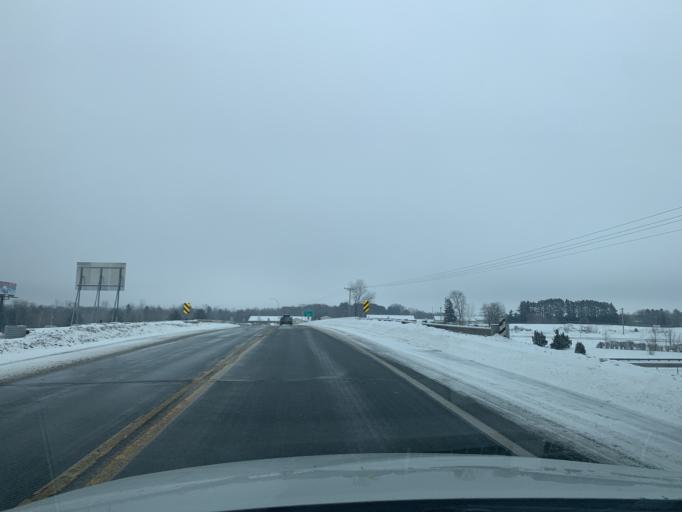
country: US
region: Minnesota
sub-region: Chisago County
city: Harris
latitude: 45.5778
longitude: -92.9936
